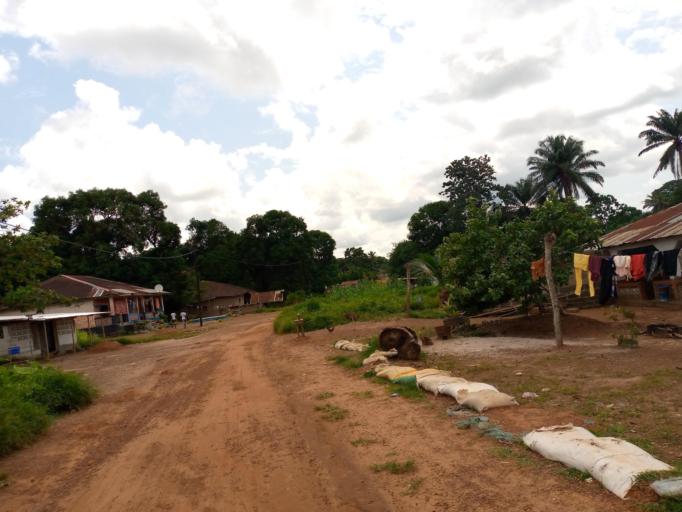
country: SL
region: Northern Province
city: Magburaka
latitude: 8.7108
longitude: -11.9333
